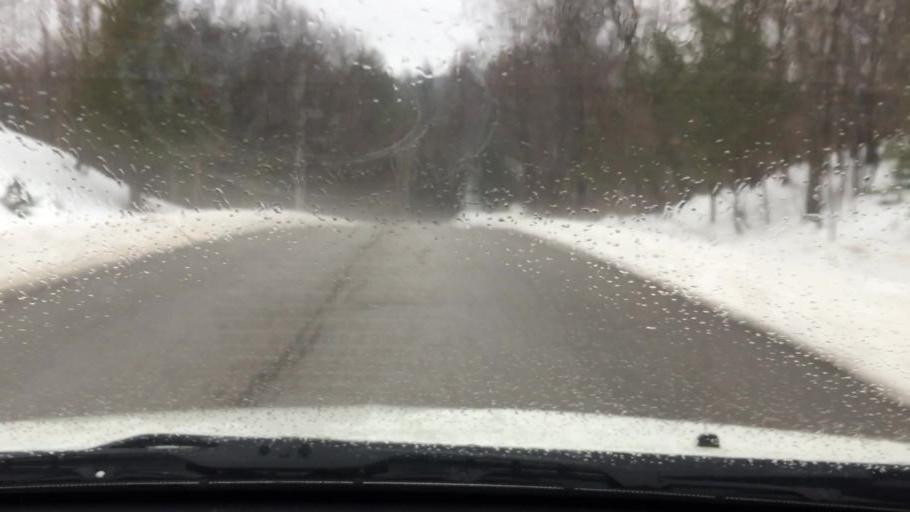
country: US
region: Michigan
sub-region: Charlevoix County
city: East Jordan
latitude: 45.1056
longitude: -85.1489
